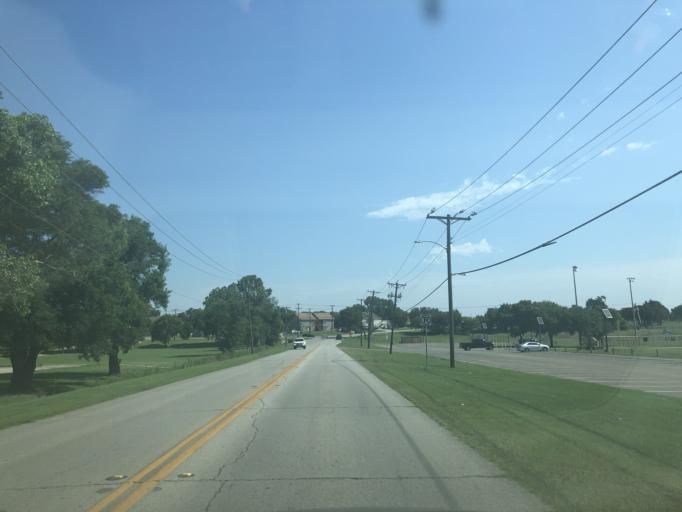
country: US
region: Texas
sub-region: Dallas County
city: Grand Prairie
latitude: 32.7266
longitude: -97.0072
